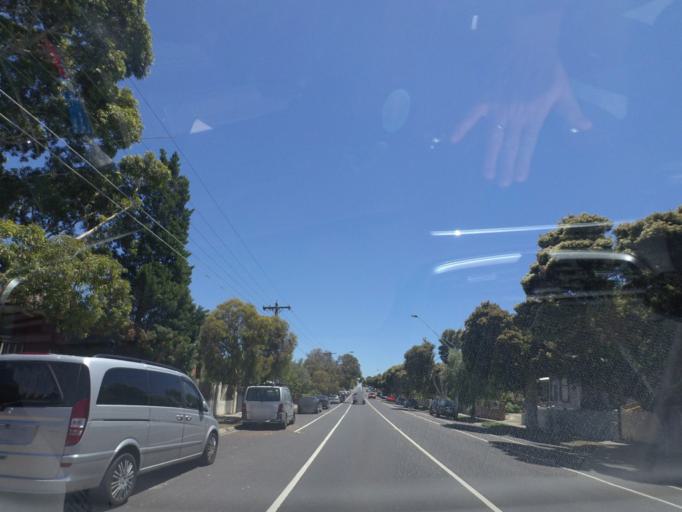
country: AU
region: Victoria
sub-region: Darebin
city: Thornbury
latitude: -37.7531
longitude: 145.0085
